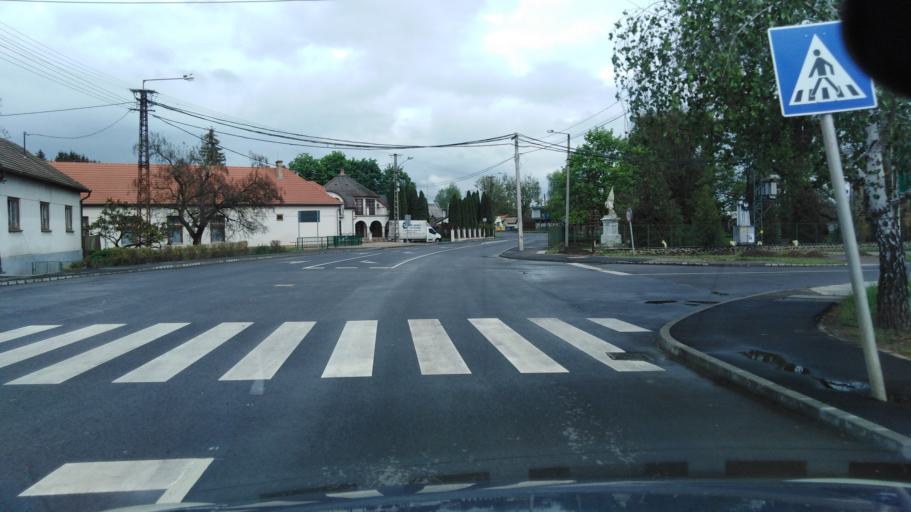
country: HU
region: Nograd
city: Szecseny
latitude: 48.1271
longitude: 19.5756
